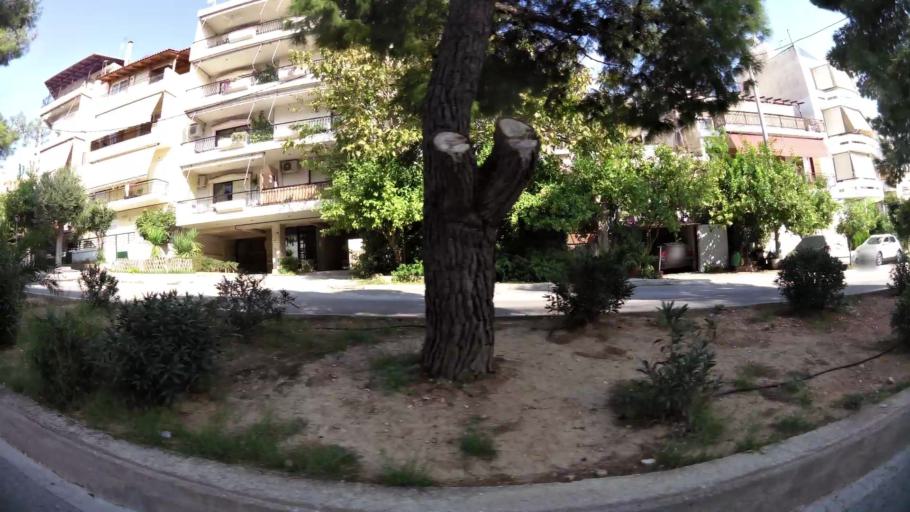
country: GR
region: Attica
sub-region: Nomarchia Athinas
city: Argyroupoli
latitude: 37.9179
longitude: 23.7537
